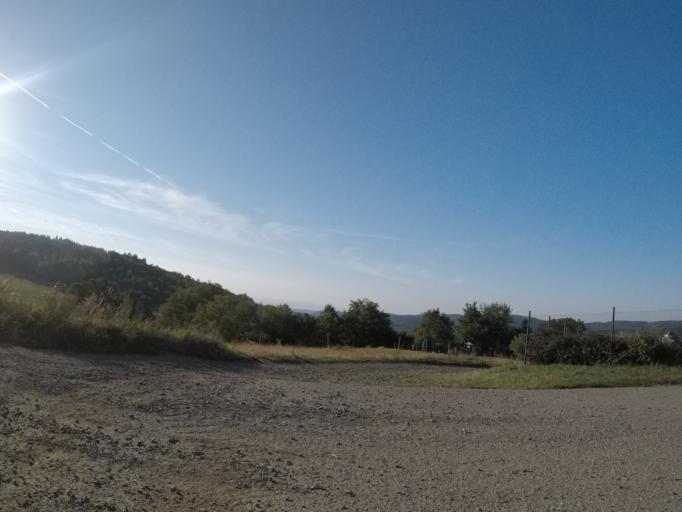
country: SK
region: Kosicky
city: Kosice
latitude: 48.7471
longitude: 21.1260
